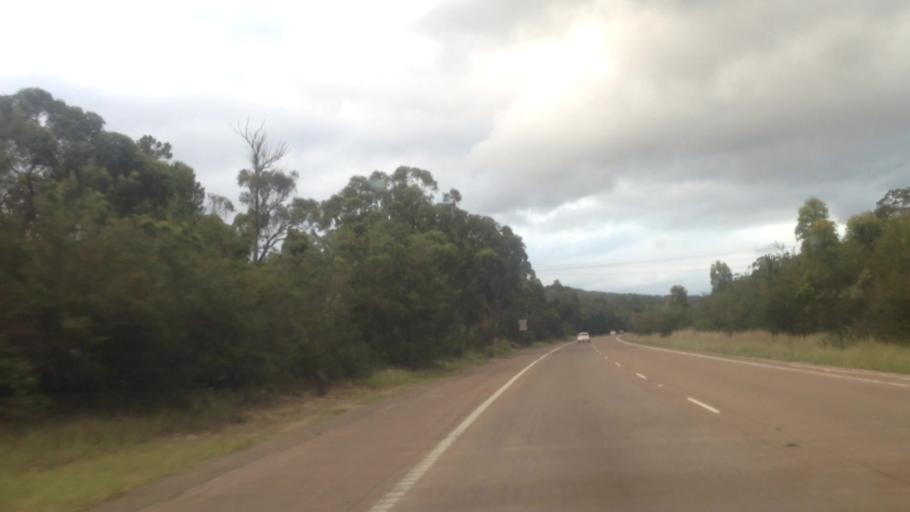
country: AU
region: New South Wales
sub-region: Wyong Shire
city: Charmhaven
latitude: -33.1757
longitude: 151.4666
